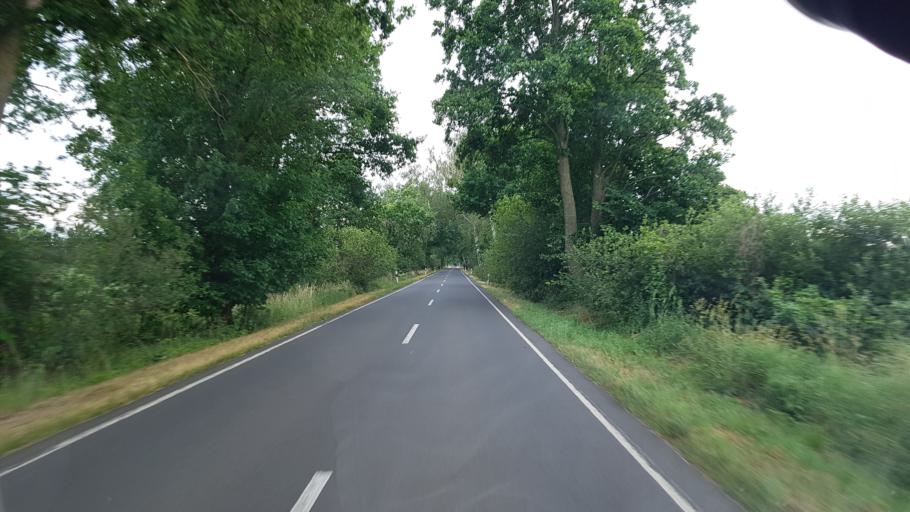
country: DE
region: Brandenburg
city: Kasel-Golzig
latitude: 51.9683
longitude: 13.6761
